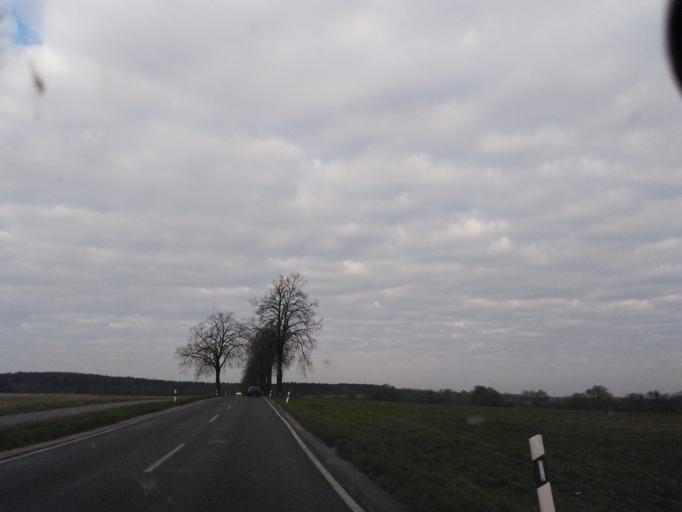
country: DE
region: Brandenburg
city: Strausberg
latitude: 52.5682
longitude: 13.9474
